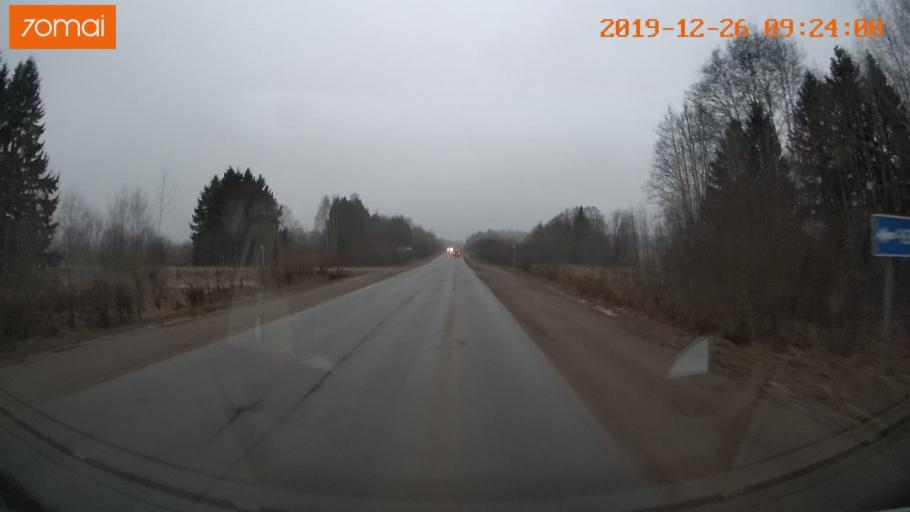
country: RU
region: Vologda
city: Gryazovets
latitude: 58.9956
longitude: 40.2035
